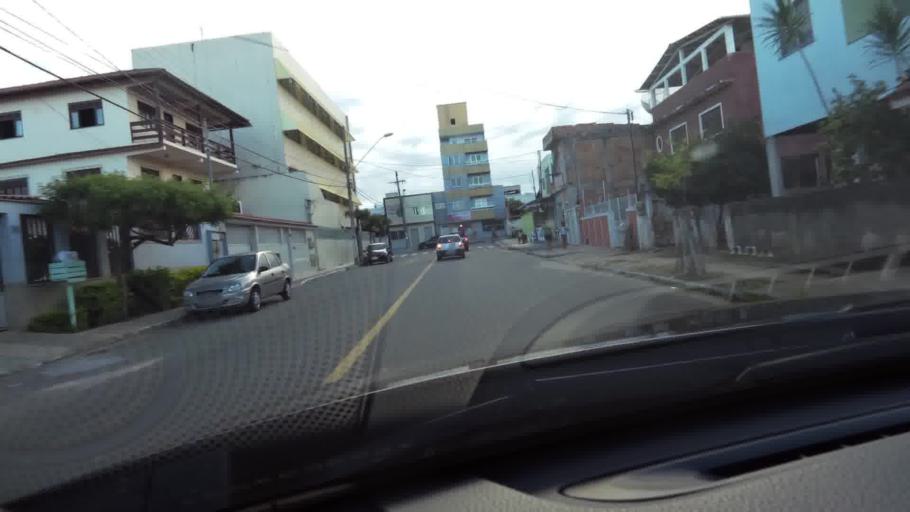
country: BR
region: Espirito Santo
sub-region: Guarapari
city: Guarapari
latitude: -20.6596
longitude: -40.5008
